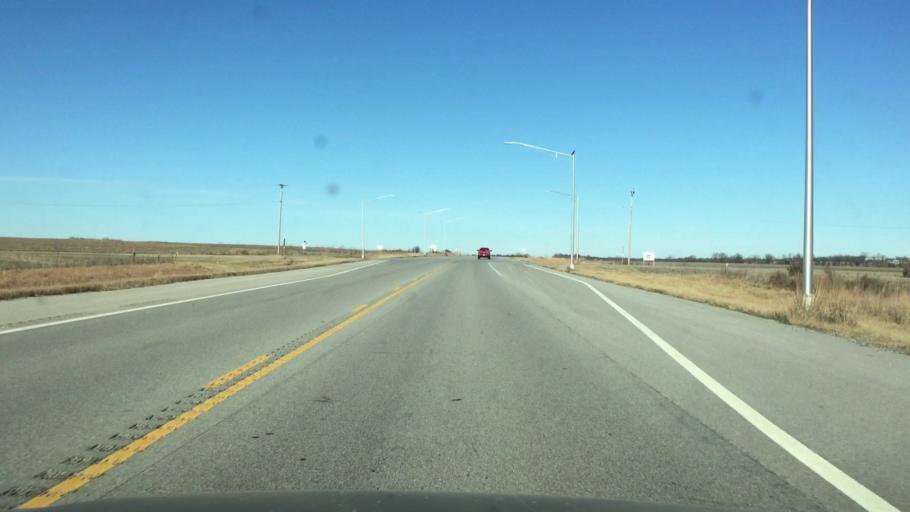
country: US
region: Kansas
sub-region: Allen County
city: Iola
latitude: 37.9503
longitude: -95.3811
